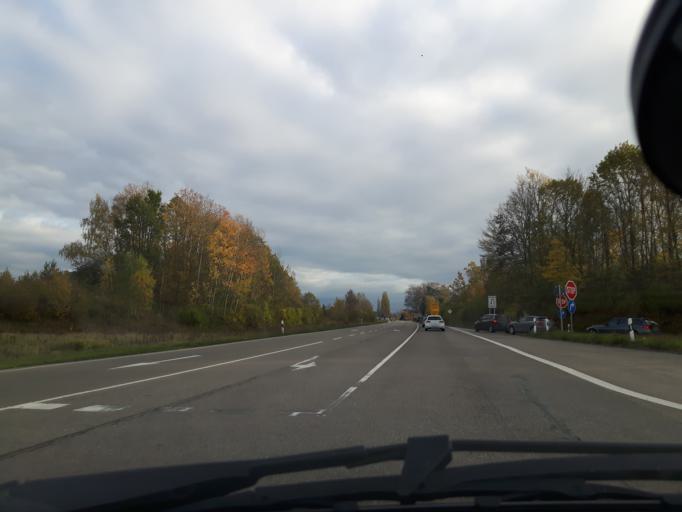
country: DE
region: Bavaria
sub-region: Regierungsbezirk Mittelfranken
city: Burgoberbach
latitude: 49.2557
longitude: 10.5897
